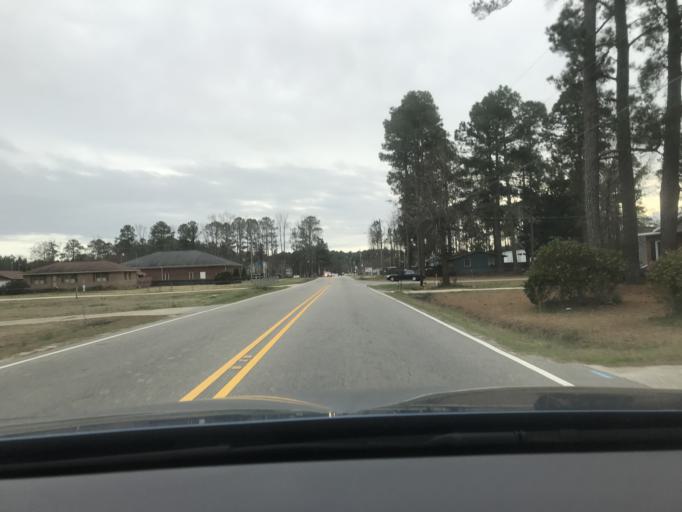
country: US
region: North Carolina
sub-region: Cumberland County
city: Fort Bragg
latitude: 35.0560
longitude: -79.0120
